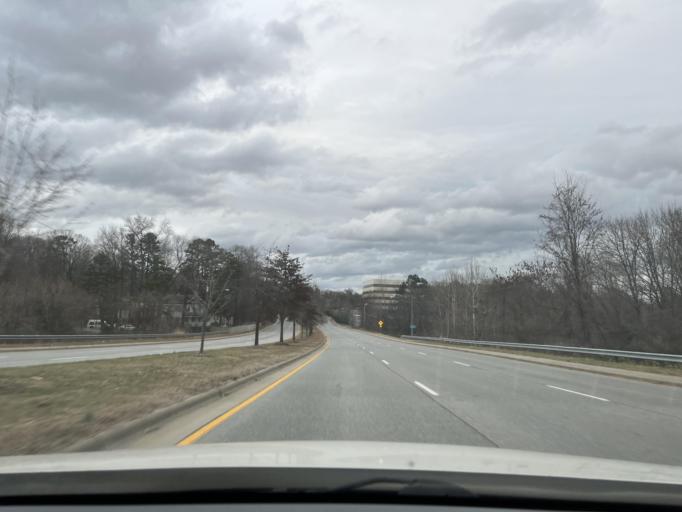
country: US
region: North Carolina
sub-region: Guilford County
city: Greensboro
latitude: 36.0475
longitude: -79.8480
